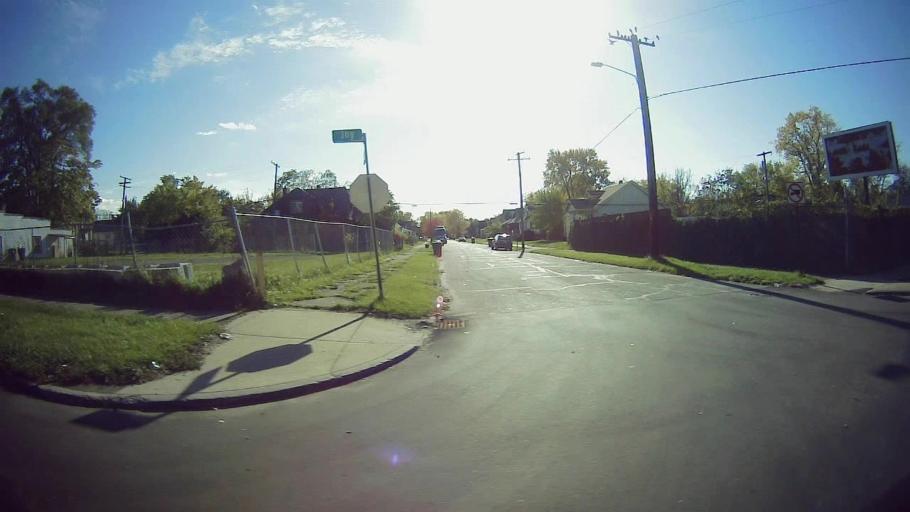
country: US
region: Michigan
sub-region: Wayne County
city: Dearborn
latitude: 42.3592
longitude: -83.1456
